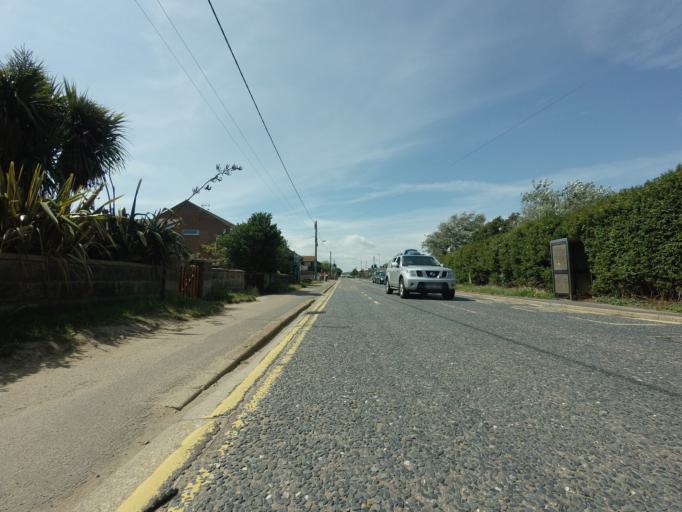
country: GB
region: England
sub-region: East Sussex
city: Rye
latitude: 50.9352
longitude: 0.7976
